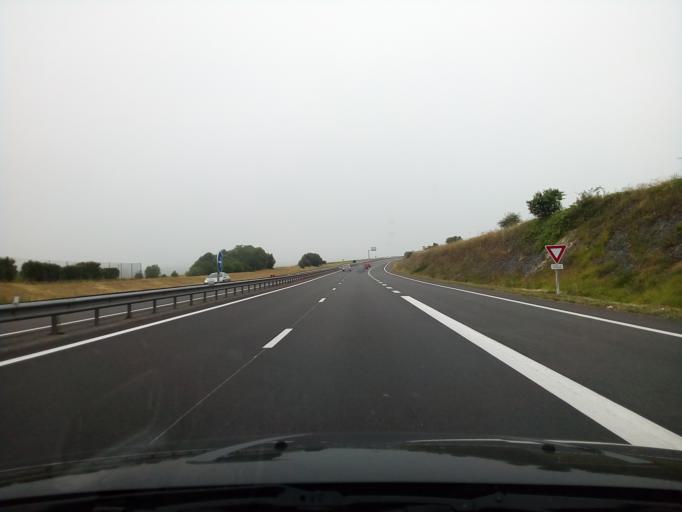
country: FR
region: Poitou-Charentes
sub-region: Departement de la Charente
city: Gensac-la-Pallue
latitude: 45.6651
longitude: -0.2349
